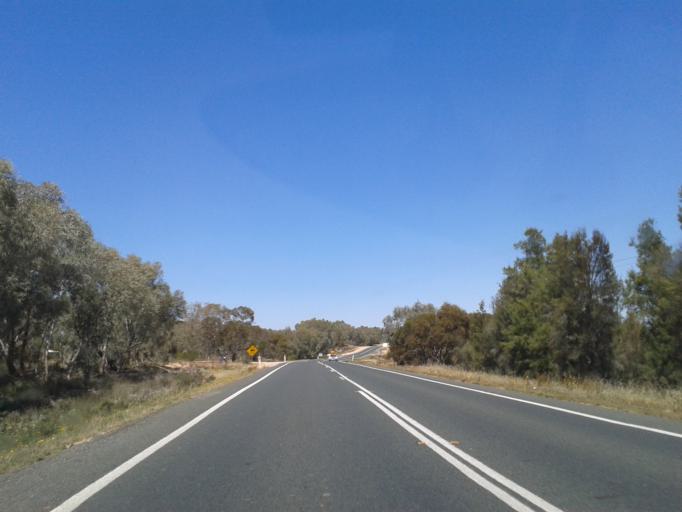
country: AU
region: New South Wales
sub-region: Wentworth
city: Gol Gol
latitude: -34.2382
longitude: 142.2493
